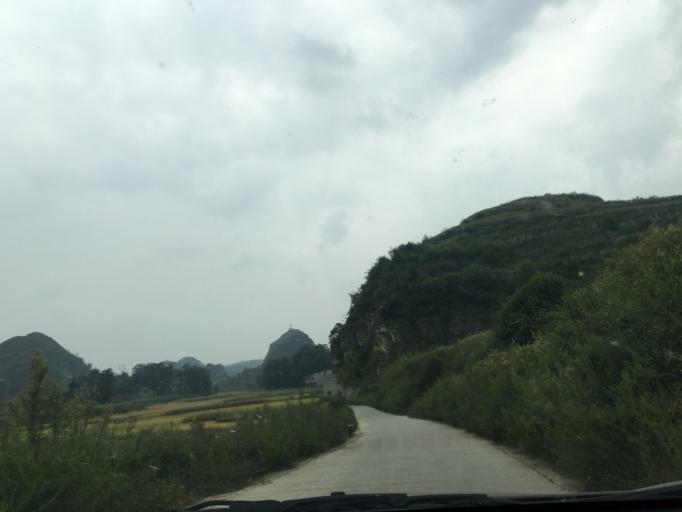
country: CN
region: Guangxi Zhuangzu Zizhiqu
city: Xinzhou
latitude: 25.5326
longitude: 105.6299
